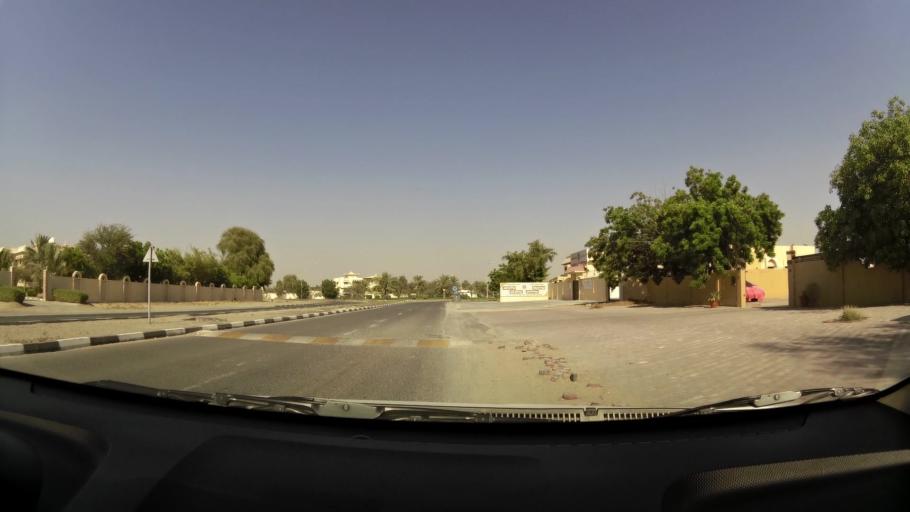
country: AE
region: Ajman
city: Ajman
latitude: 25.4086
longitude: 55.4640
